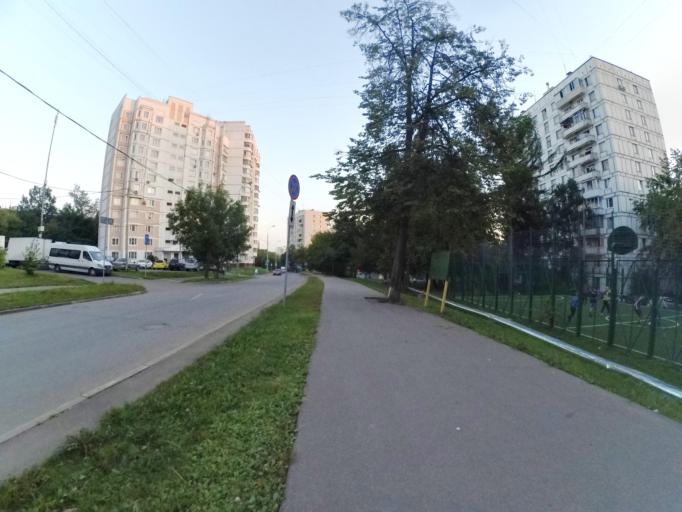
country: RU
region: Moscow
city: Strogino
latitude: 55.8451
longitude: 37.3988
